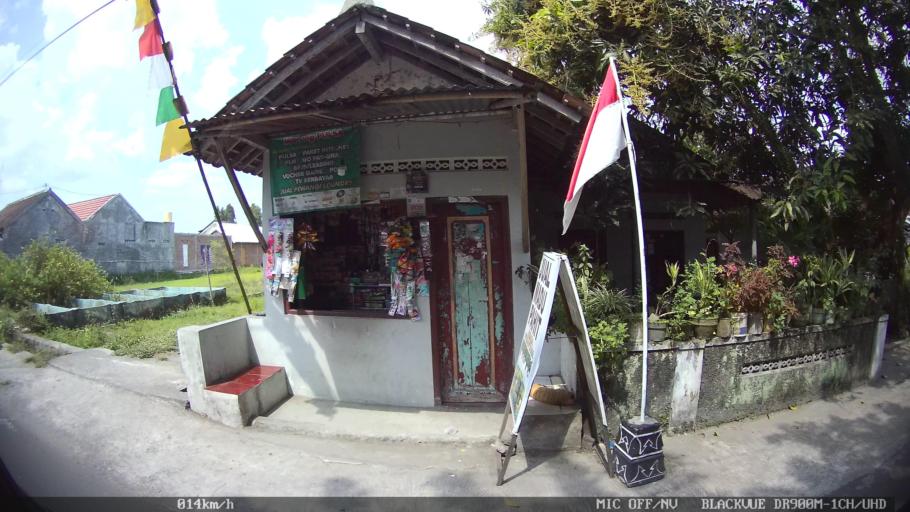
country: ID
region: Daerah Istimewa Yogyakarta
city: Kasihan
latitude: -7.8176
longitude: 110.3384
